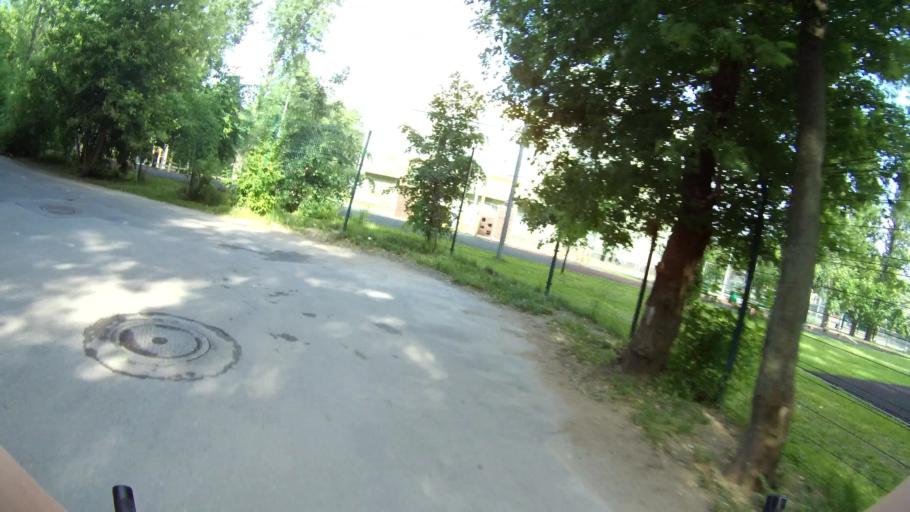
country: RU
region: Moscow
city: Ryazanskiy
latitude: 55.7391
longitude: 37.7401
